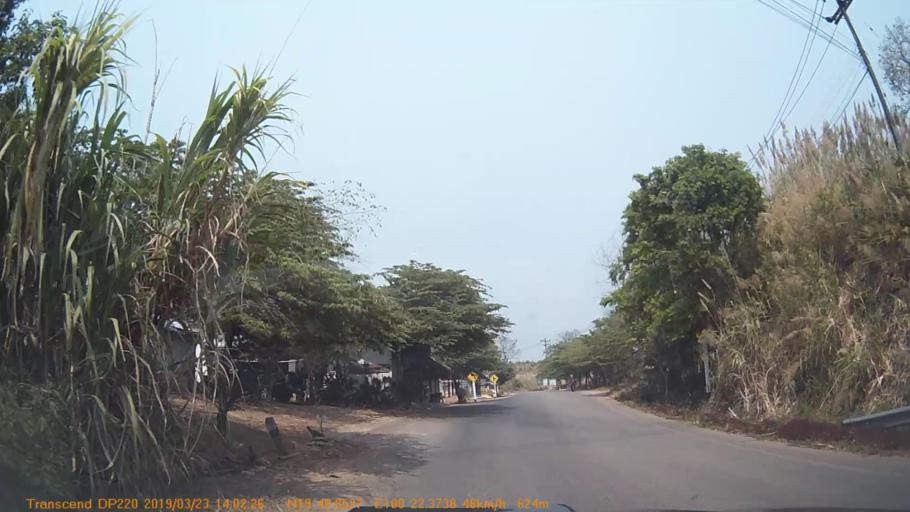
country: TH
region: Chiang Rai
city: Khun Tan
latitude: 19.8307
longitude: 100.3723
